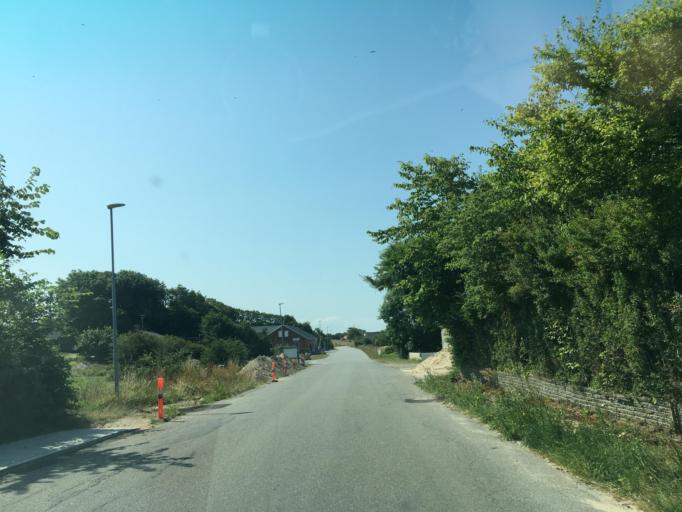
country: DK
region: North Denmark
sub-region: Thisted Kommune
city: Hurup
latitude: 56.8176
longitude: 8.4855
